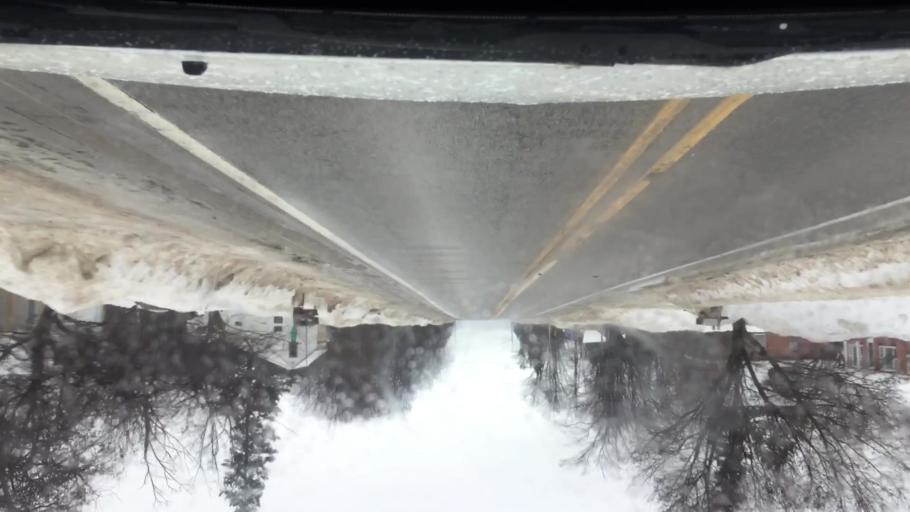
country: US
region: Michigan
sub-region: Charlevoix County
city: East Jordan
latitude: 45.1460
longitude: -85.1398
